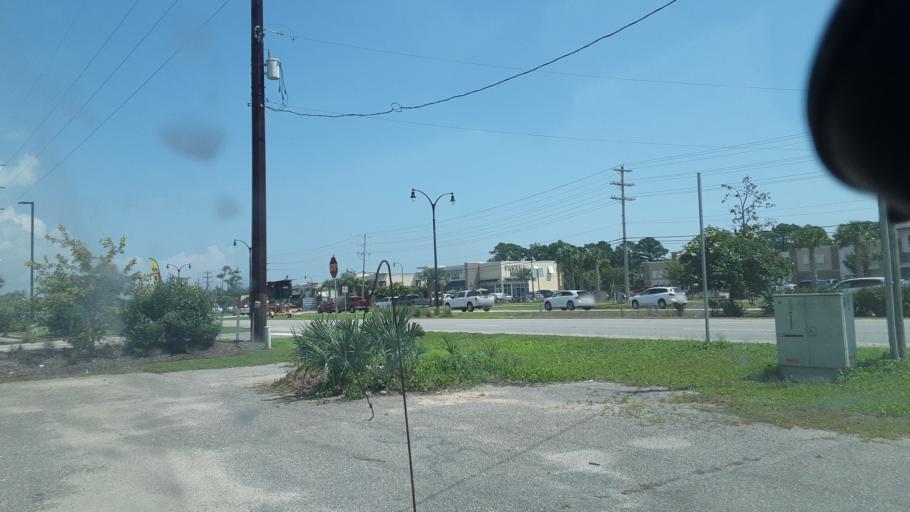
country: US
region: South Carolina
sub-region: Horry County
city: North Myrtle Beach
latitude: 33.8404
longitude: -78.6653
